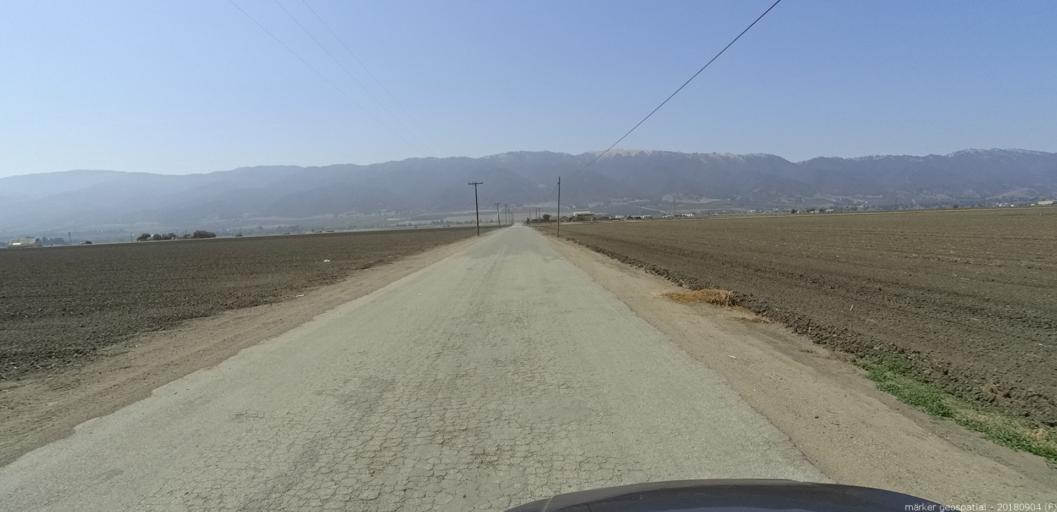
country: US
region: California
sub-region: Monterey County
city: Gonzales
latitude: 36.5113
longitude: -121.4711
